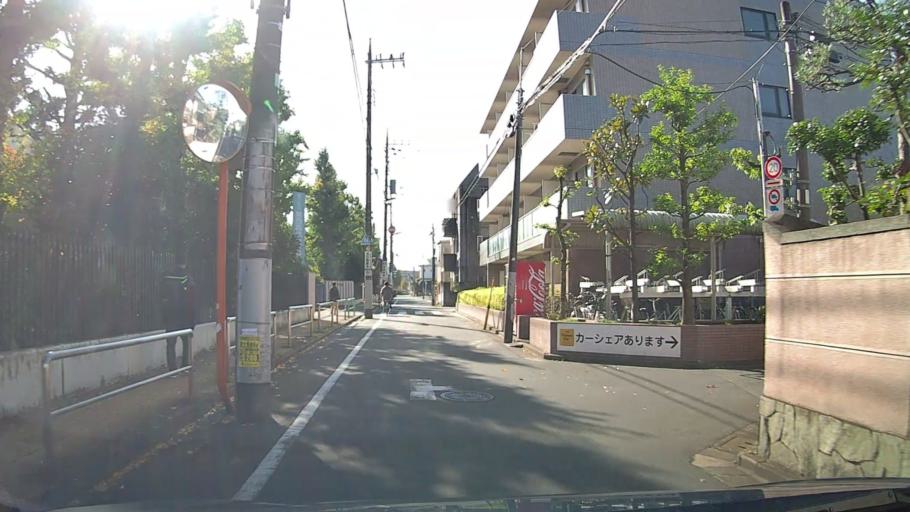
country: JP
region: Saitama
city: Wako
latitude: 35.7396
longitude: 139.6259
